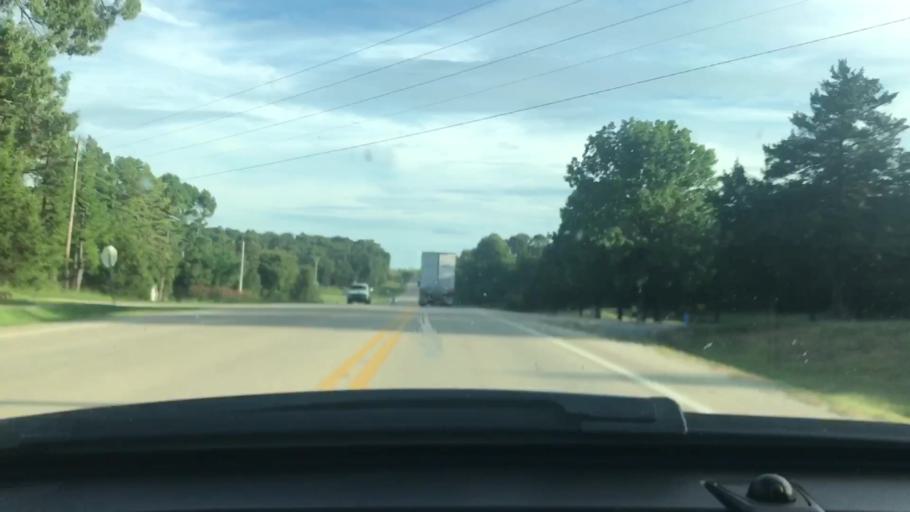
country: US
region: Arkansas
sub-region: Lawrence County
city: Hoxie
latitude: 36.1551
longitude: -91.1616
